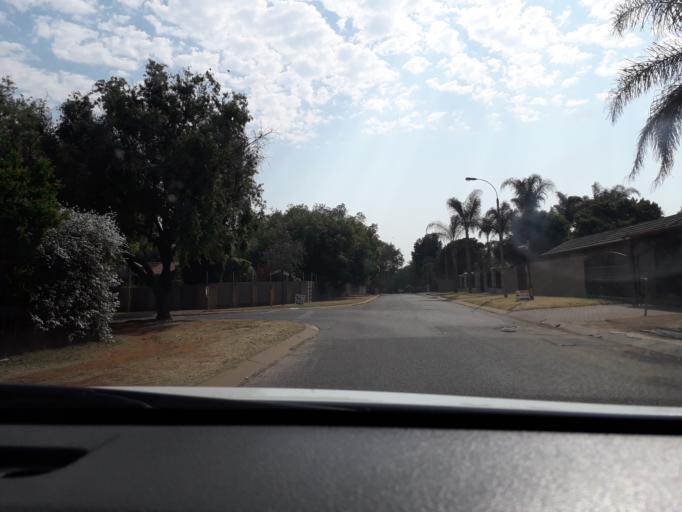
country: ZA
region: Gauteng
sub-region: City of Johannesburg Metropolitan Municipality
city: Modderfontein
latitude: -26.0816
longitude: 28.2416
